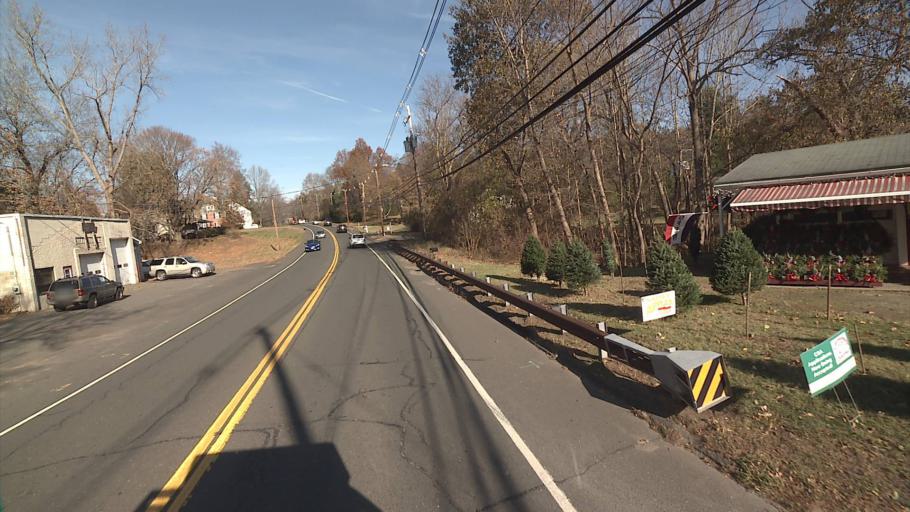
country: US
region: Connecticut
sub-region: Hartford County
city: Glastonbury Center
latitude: 41.6736
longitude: -72.5993
